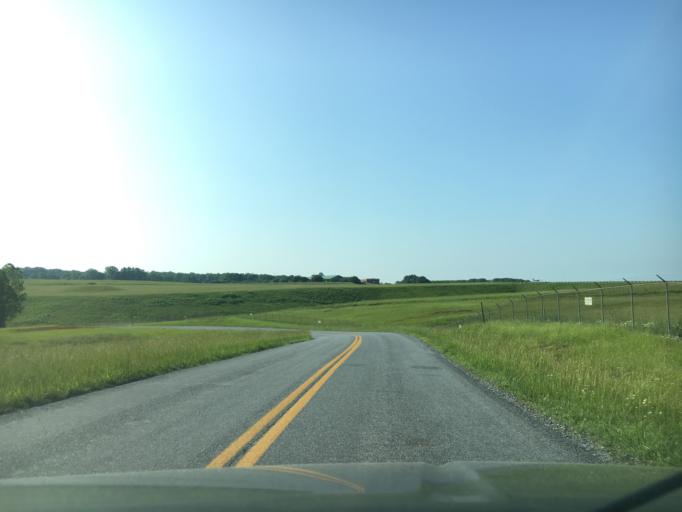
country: US
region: Virginia
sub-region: Campbell County
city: Timberlake
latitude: 37.3357
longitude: -79.1985
